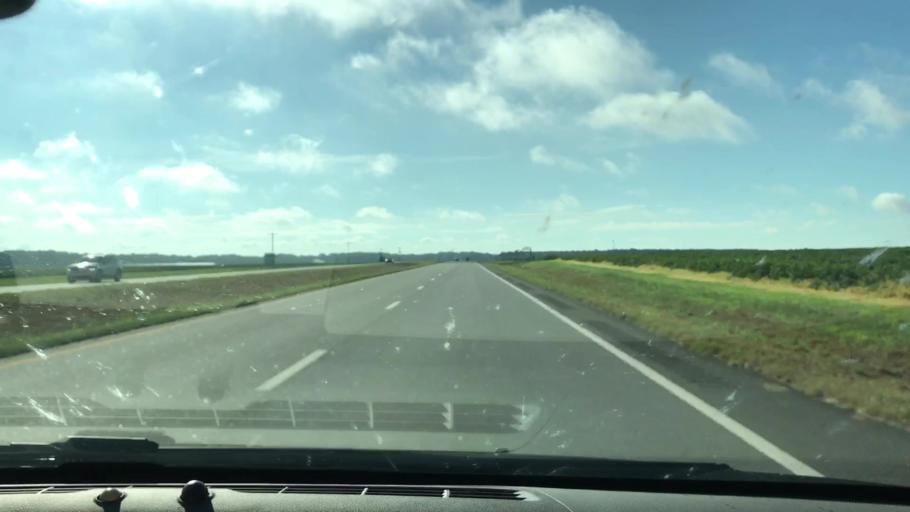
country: US
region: Georgia
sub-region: Terrell County
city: Dawson
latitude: 31.7032
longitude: -84.3300
